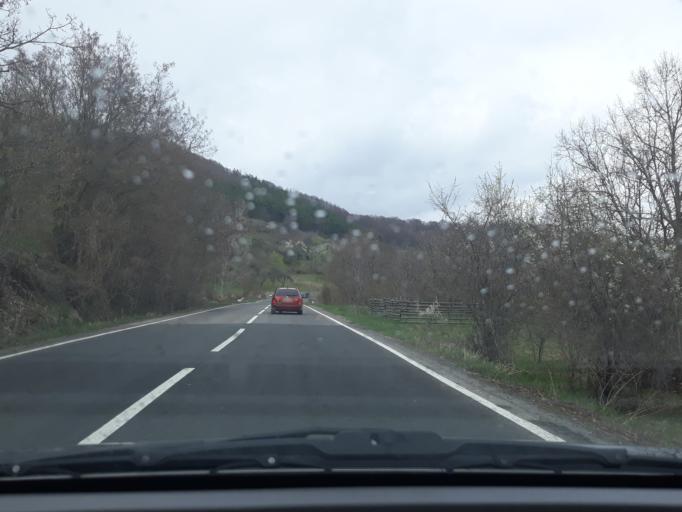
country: RO
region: Harghita
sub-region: Comuna Lupeni
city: Lupeni
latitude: 46.4094
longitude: 25.2185
